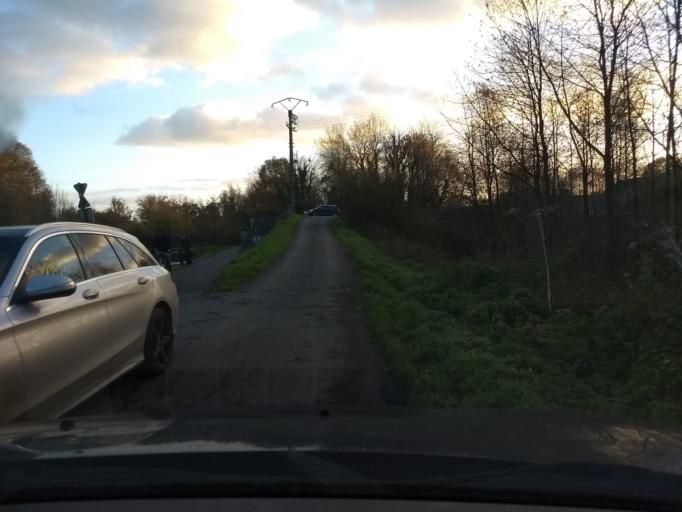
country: BE
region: Wallonia
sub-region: Province du Brabant Wallon
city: Ittre
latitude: 50.5897
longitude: 4.2524
